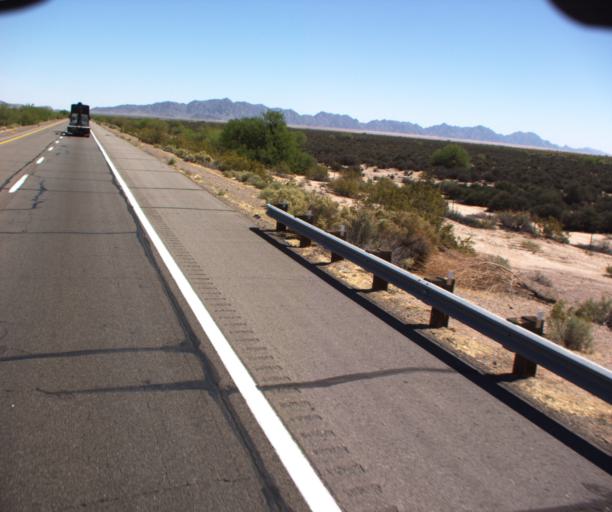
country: US
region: Arizona
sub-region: Yuma County
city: Wellton
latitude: 32.7043
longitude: -113.8816
